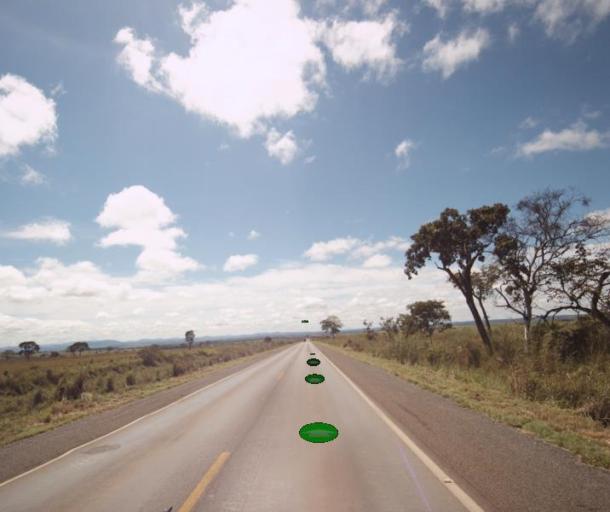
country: BR
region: Goias
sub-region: Padre Bernardo
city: Padre Bernardo
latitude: -15.1751
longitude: -48.4019
